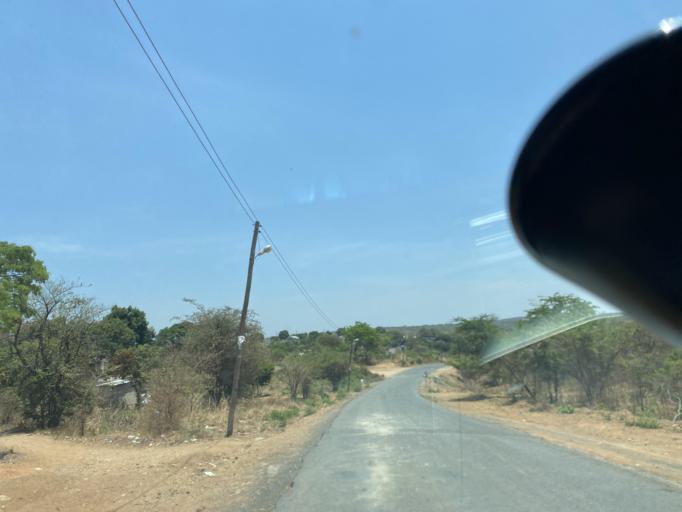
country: ZM
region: Lusaka
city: Kafue
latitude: -15.8678
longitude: 28.4378
